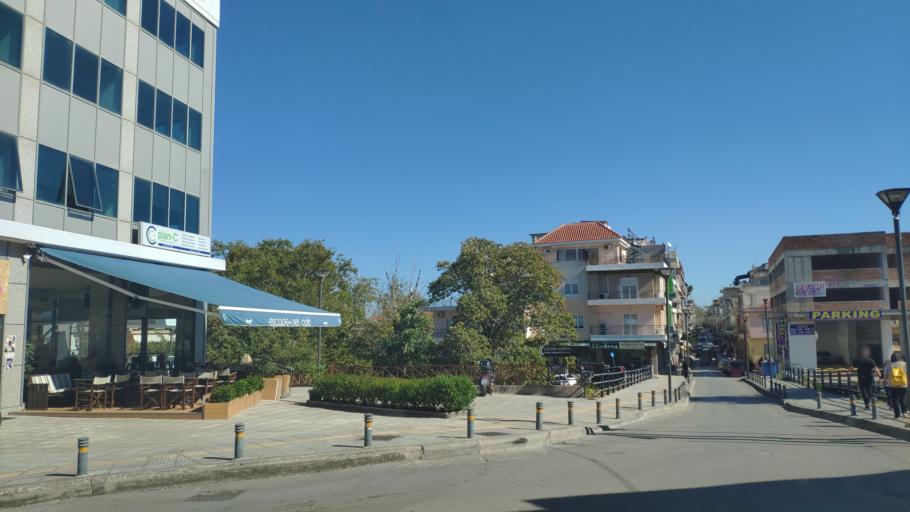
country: GR
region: Central Greece
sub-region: Nomos Voiotias
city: Livadeia
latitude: 38.4384
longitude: 22.8731
